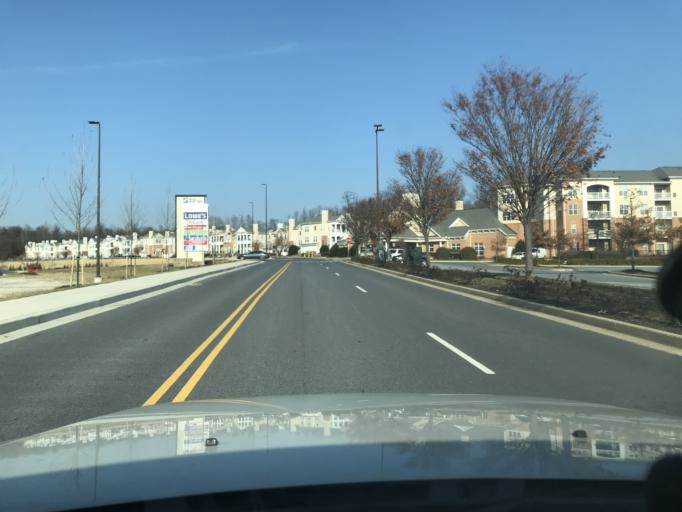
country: US
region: Maryland
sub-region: Baltimore County
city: Owings Mills
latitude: 39.4059
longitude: -76.7869
